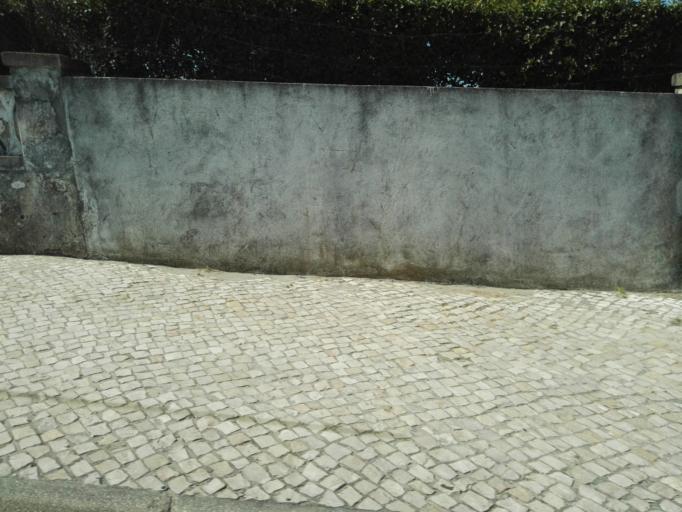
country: PT
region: Santarem
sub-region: Benavente
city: Samora Correia
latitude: 38.9369
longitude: -8.8672
